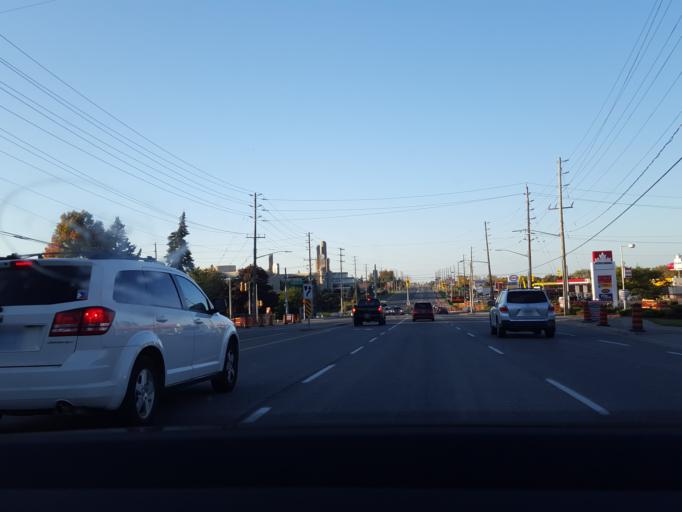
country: CA
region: Ontario
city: Newmarket
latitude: 44.0445
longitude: -79.4778
